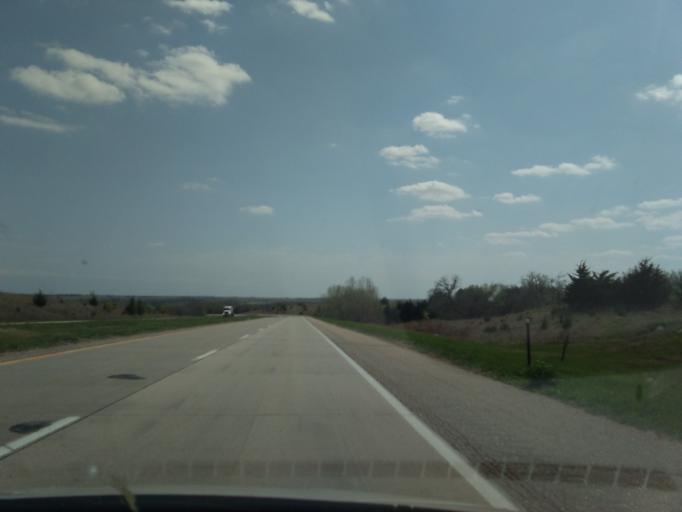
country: US
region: Nebraska
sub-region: Thayer County
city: Hebron
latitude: 40.1742
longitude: -97.5744
